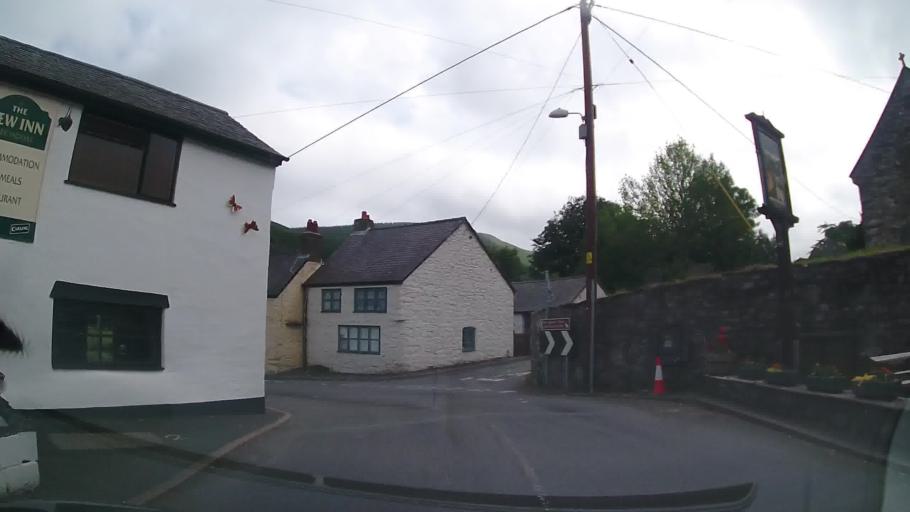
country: GB
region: Wales
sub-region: Sir Powys
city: Llangynog
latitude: 52.8243
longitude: -3.4063
